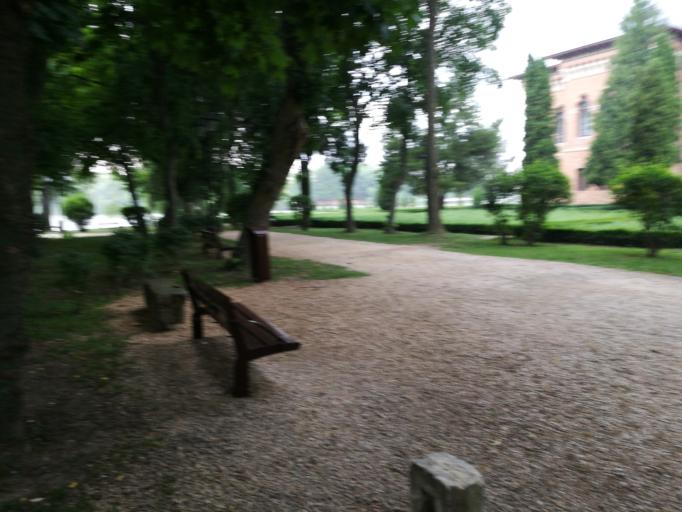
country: RO
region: Ilfov
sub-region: Comuna Mogosoaia
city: Mogosoaia
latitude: 44.5271
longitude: 25.9931
